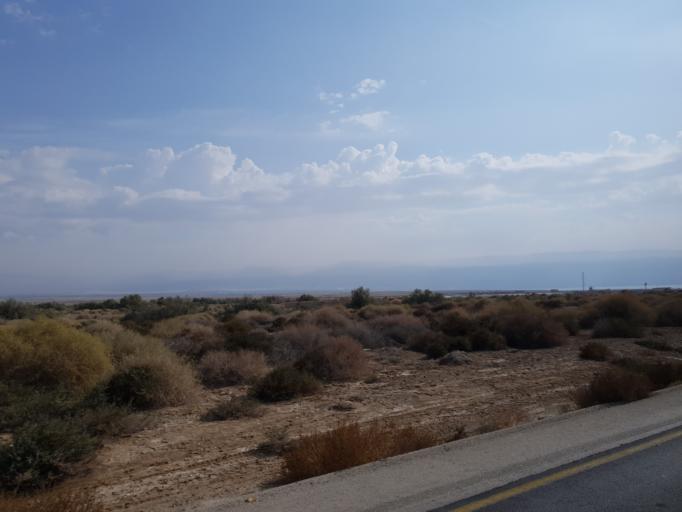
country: PS
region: West Bank
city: Jericho
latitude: 31.7816
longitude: 35.5020
